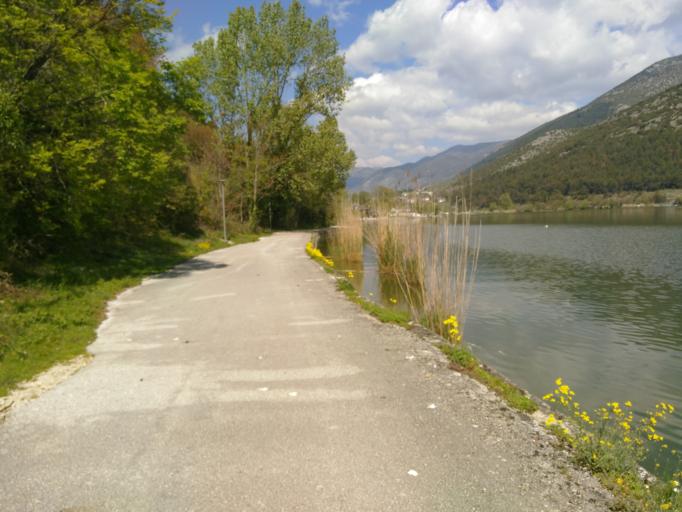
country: GR
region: Epirus
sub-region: Nomos Ioanninon
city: Ioannina
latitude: 39.6774
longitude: 20.8779
